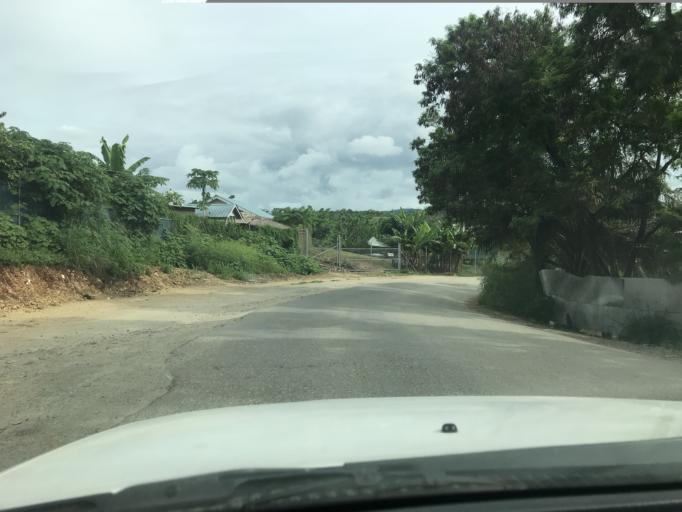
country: SB
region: Guadalcanal
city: Honiara
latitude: -9.4364
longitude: 159.9451
